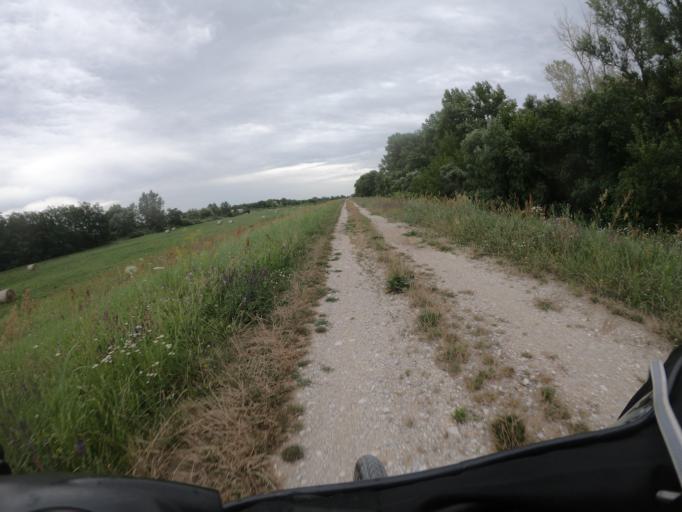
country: HU
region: Jasz-Nagykun-Szolnok
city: Tiszafured
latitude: 47.6853
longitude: 20.7940
